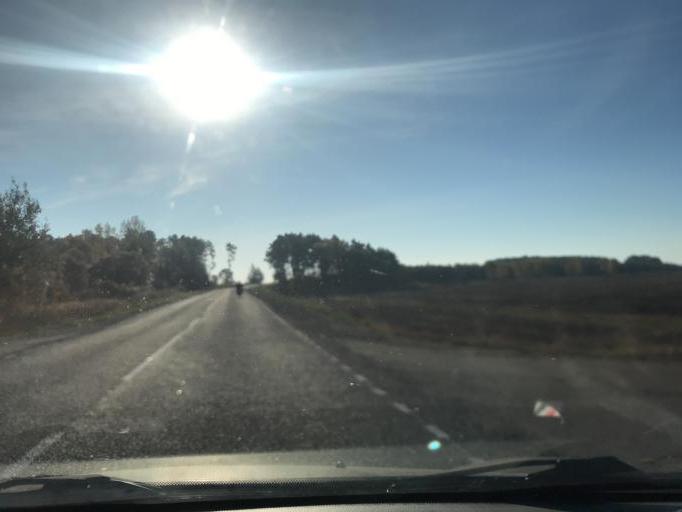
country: BY
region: Gomel
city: Brahin
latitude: 51.7701
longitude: 30.2982
